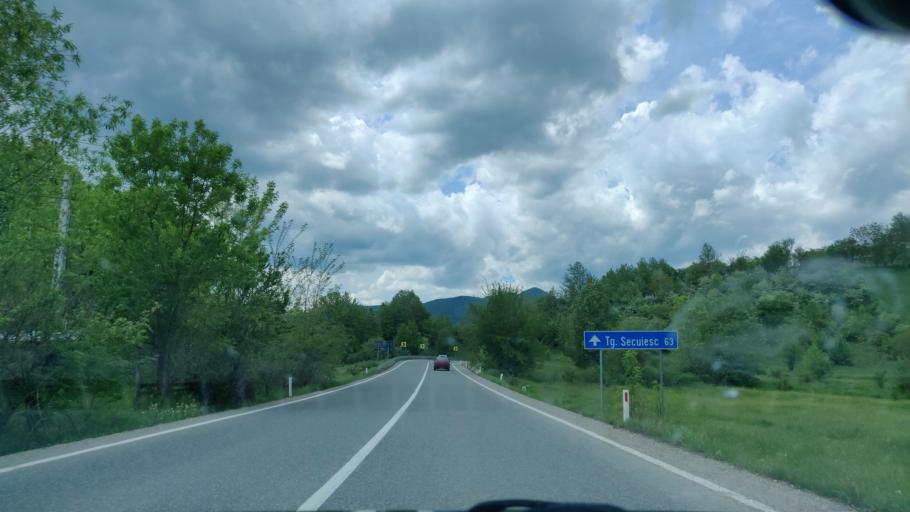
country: RO
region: Vrancea
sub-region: Comuna Negrilesti
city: Negrilesti
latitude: 45.9220
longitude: 26.7039
